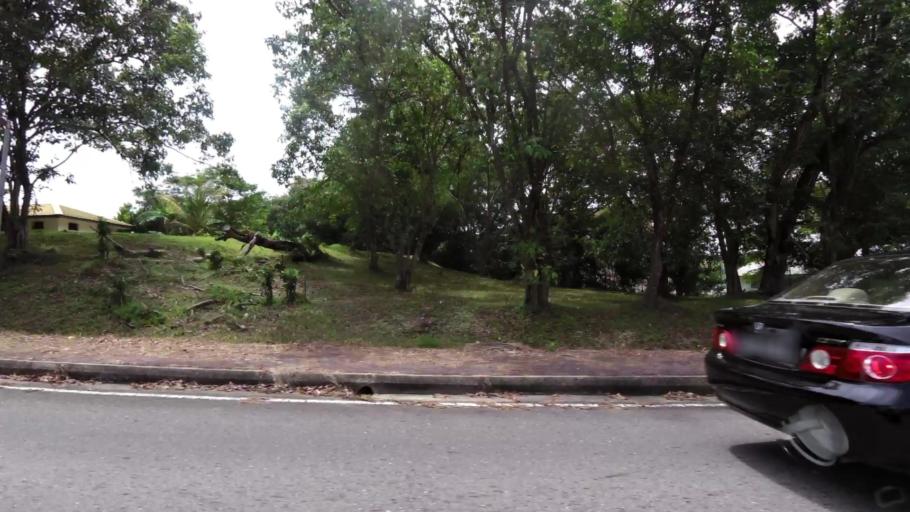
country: BN
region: Brunei and Muara
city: Bandar Seri Begawan
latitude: 4.9040
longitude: 114.9154
